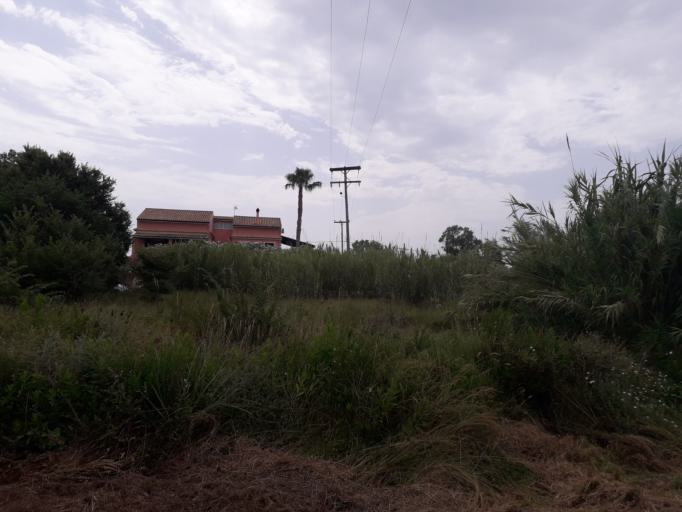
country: GR
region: Ionian Islands
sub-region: Nomos Kerkyras
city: Perivoli
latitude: 39.4301
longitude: 19.9507
